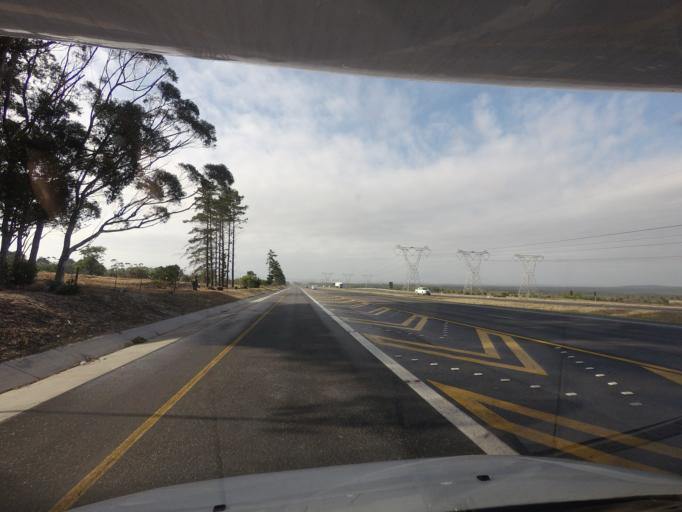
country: ZA
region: Western Cape
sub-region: City of Cape Town
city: Sunset Beach
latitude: -33.7267
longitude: 18.5448
